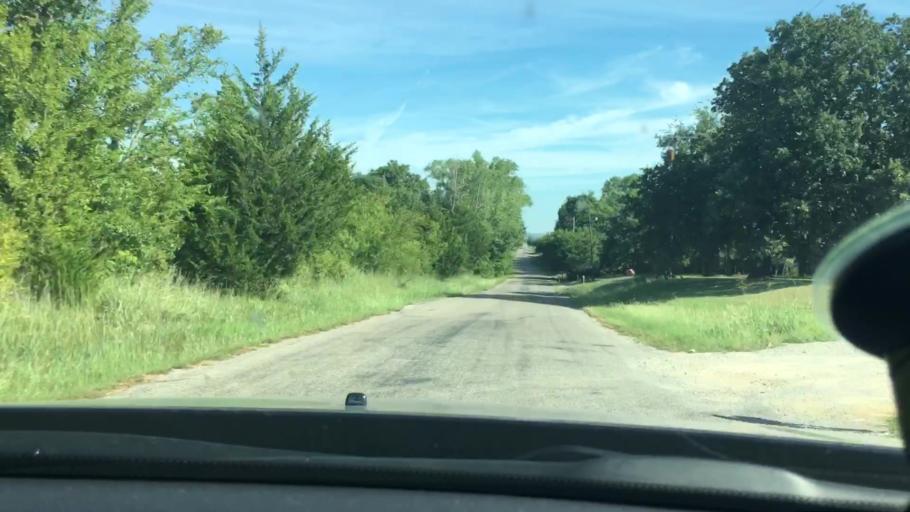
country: US
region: Oklahoma
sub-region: Carter County
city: Lone Grove
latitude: 34.2530
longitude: -97.2474
